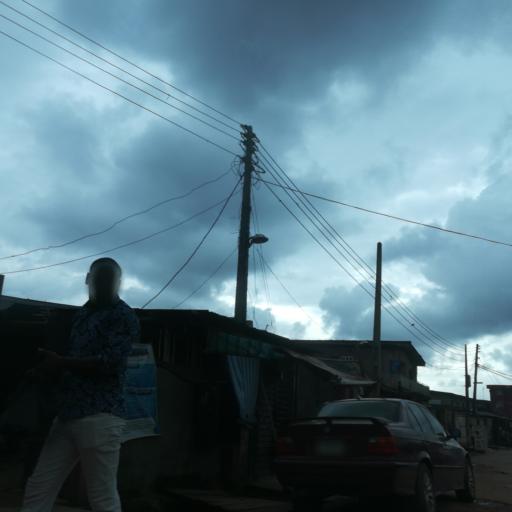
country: NG
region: Lagos
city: Agege
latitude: 6.6105
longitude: 3.2968
